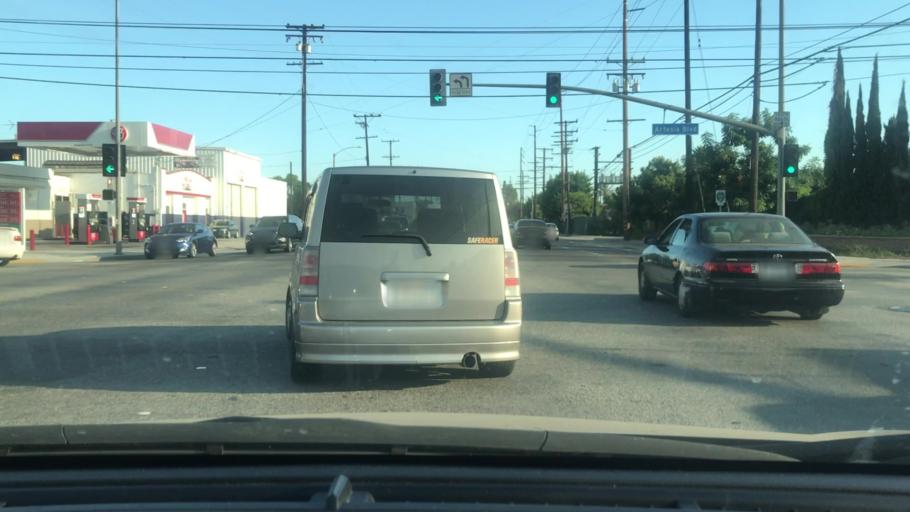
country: US
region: California
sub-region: Los Angeles County
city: Paramount
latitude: 33.8748
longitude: -118.1600
